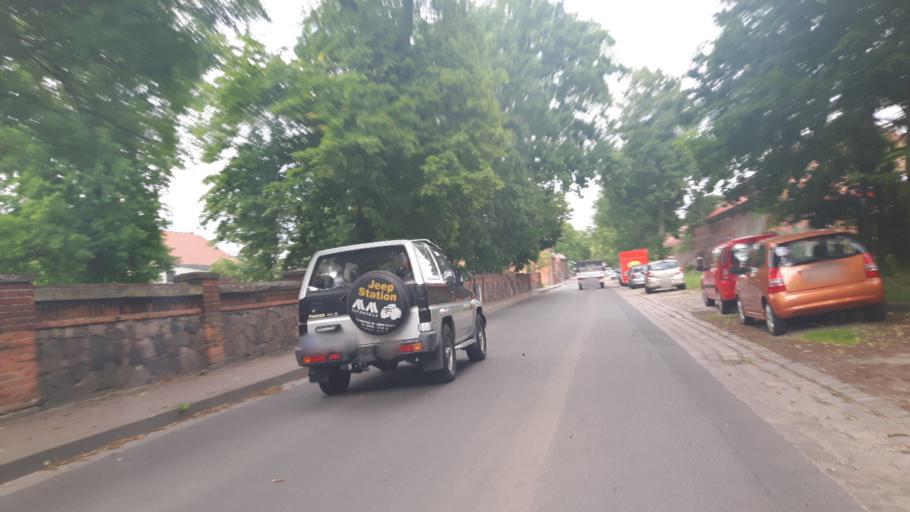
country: DE
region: Brandenburg
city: Bernau bei Berlin
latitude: 52.6613
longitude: 13.6337
